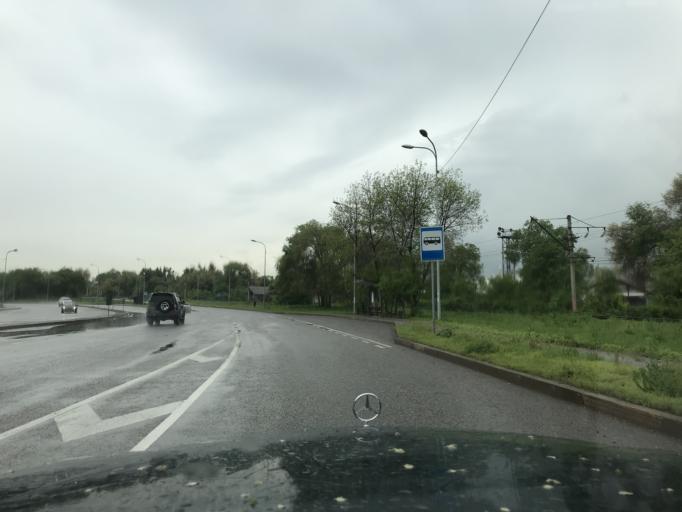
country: KZ
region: Almaty Oblysy
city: Pervomayskiy
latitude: 43.3340
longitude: 76.9612
